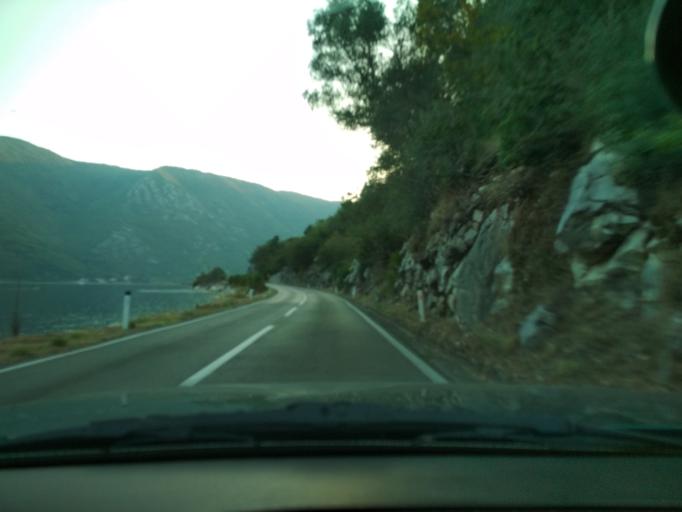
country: ME
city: Lipci
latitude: 42.5028
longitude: 18.6654
